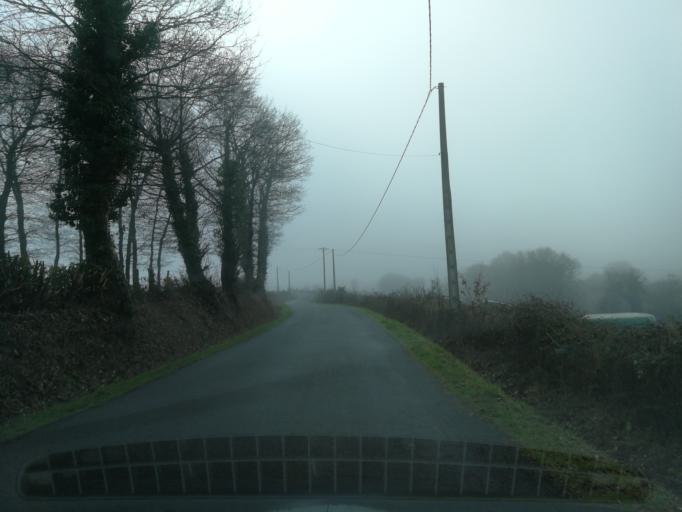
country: FR
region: Brittany
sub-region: Departement du Morbihan
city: La Vraie-Croix
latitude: 47.7249
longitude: -2.5103
